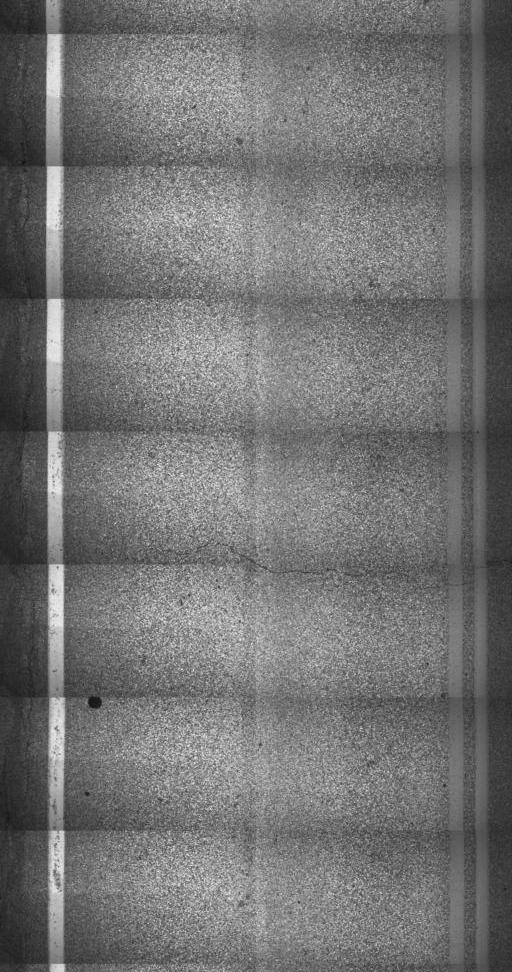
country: US
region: Vermont
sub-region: Windsor County
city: Chester
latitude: 43.3650
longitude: -72.7208
